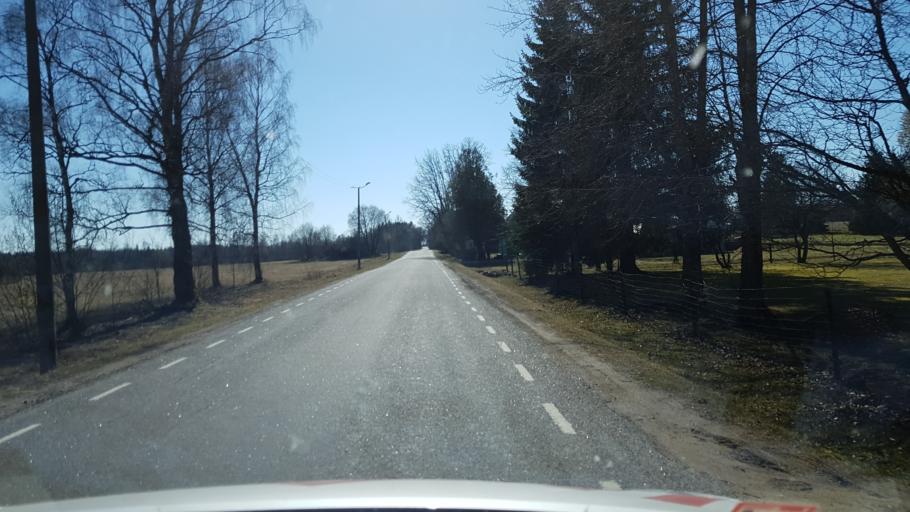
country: EE
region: Laeaene-Virumaa
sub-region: Tamsalu vald
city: Tamsalu
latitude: 59.0884
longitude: 26.1686
